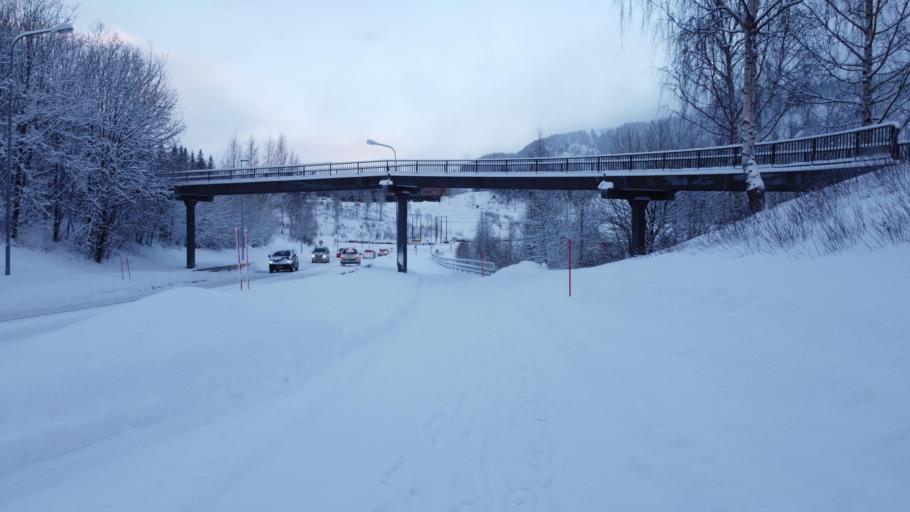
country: NO
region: Nordland
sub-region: Rana
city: Mo i Rana
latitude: 66.3262
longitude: 14.1592
